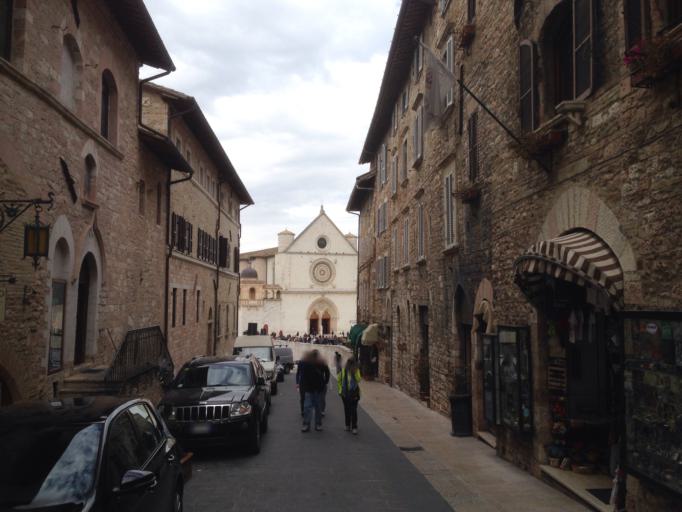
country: IT
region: Umbria
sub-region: Provincia di Perugia
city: Assisi
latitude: 43.0737
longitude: 12.6076
